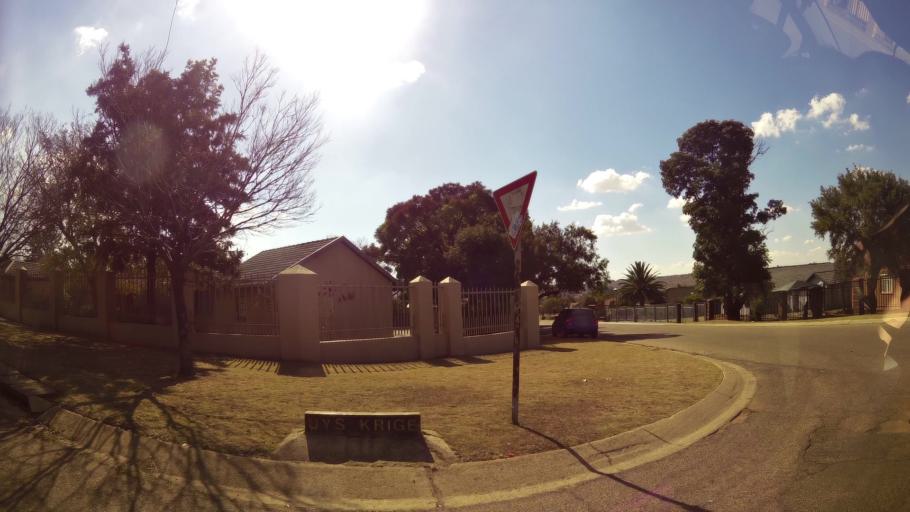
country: ZA
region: Mpumalanga
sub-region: Nkangala District Municipality
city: Witbank
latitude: -25.9449
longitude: 29.2487
